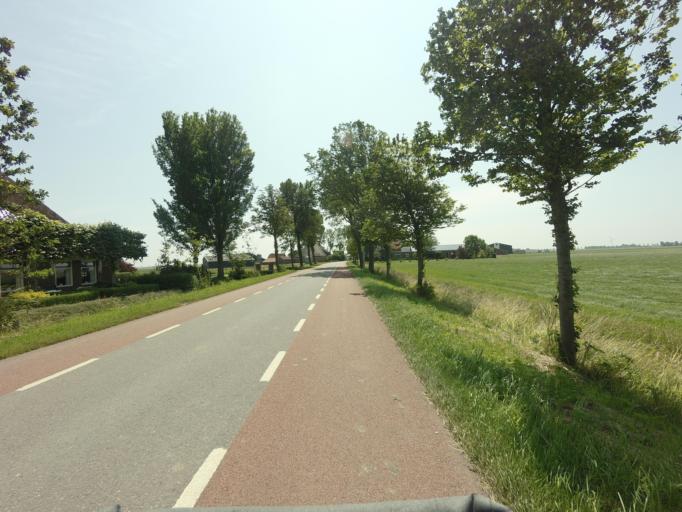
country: NL
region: North Holland
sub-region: Gemeente Opmeer
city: Opmeer
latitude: 52.6892
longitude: 4.9427
